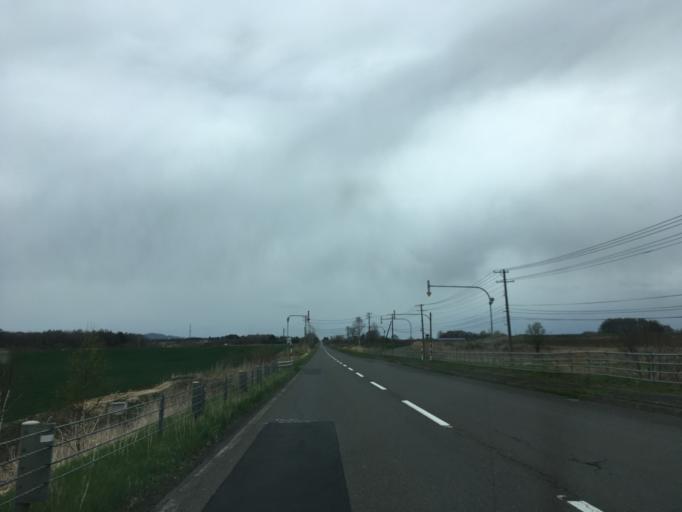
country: JP
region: Hokkaido
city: Chitose
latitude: 42.9050
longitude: 141.8126
